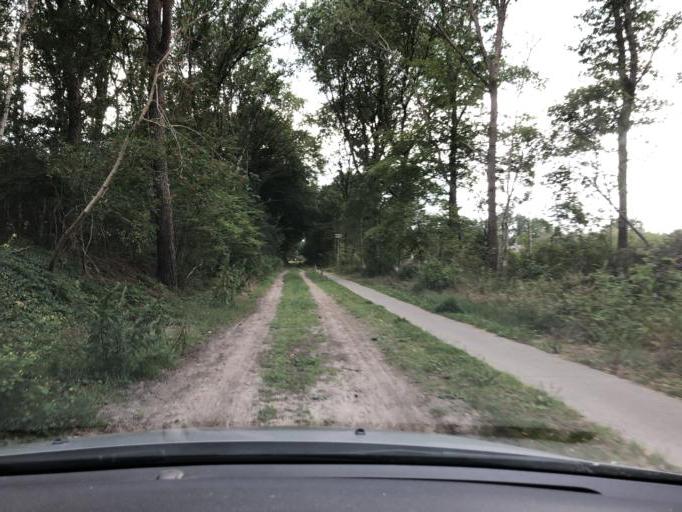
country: NL
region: Drenthe
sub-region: Gemeente Hoogeveen
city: Hoogeveen
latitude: 52.6101
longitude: 6.3750
